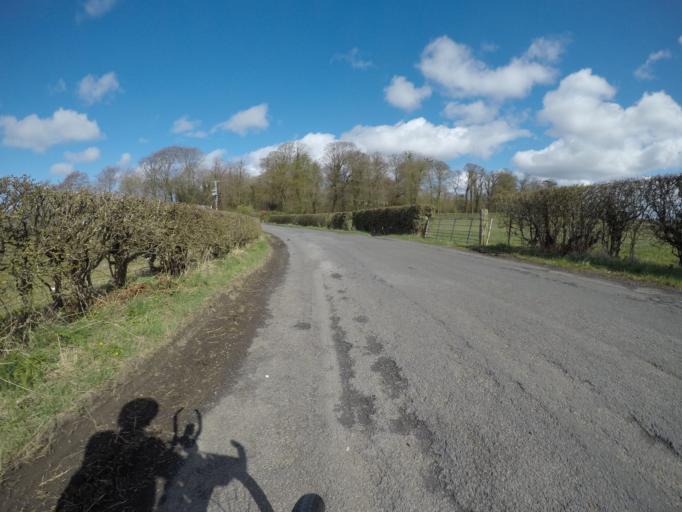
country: GB
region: Scotland
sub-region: East Ayrshire
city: Crosshouse
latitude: 55.6107
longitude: -4.5756
